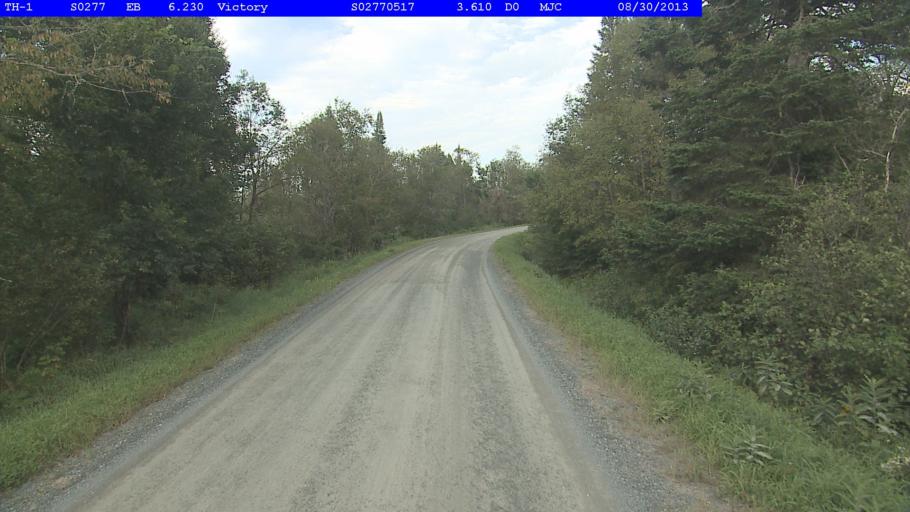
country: US
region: Vermont
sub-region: Caledonia County
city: Lyndonville
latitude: 44.5301
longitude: -71.8062
